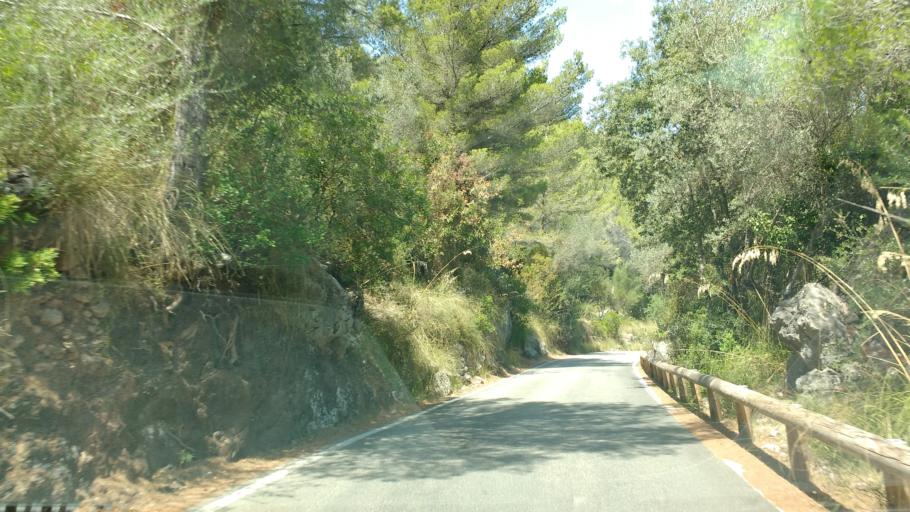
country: ES
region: Balearic Islands
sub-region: Illes Balears
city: Escorca
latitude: 39.8400
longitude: 2.7958
